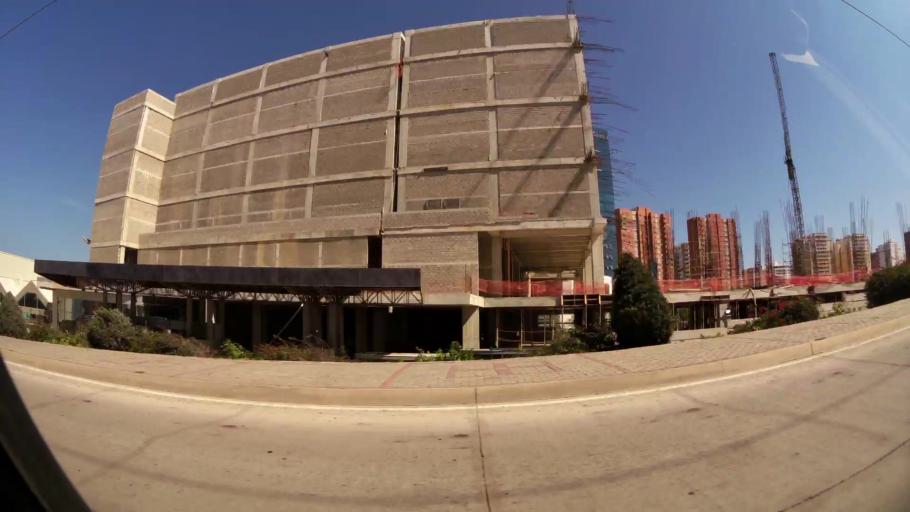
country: CO
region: Atlantico
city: Barranquilla
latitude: 11.0150
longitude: -74.8284
